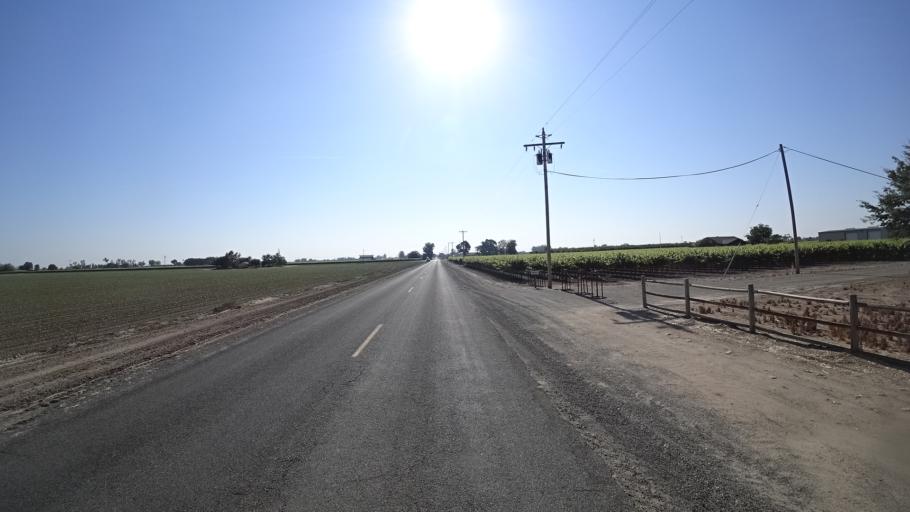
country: US
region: California
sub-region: Fresno County
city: Riverdale
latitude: 36.3656
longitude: -119.8543
